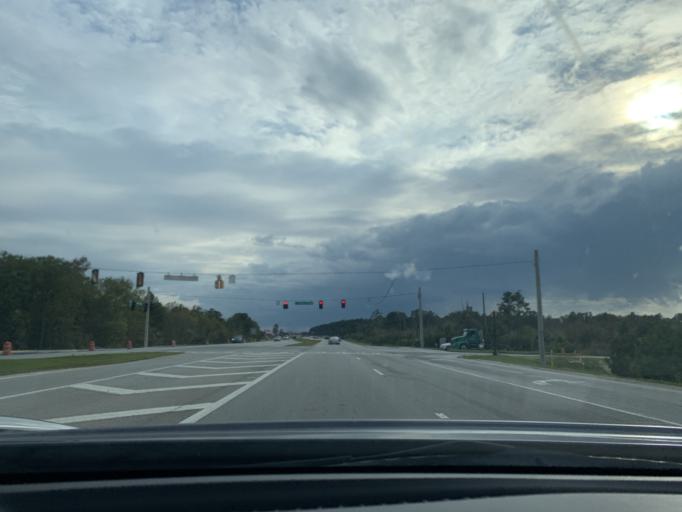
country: US
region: Georgia
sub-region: Chatham County
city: Pooler
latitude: 32.1025
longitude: -81.2686
